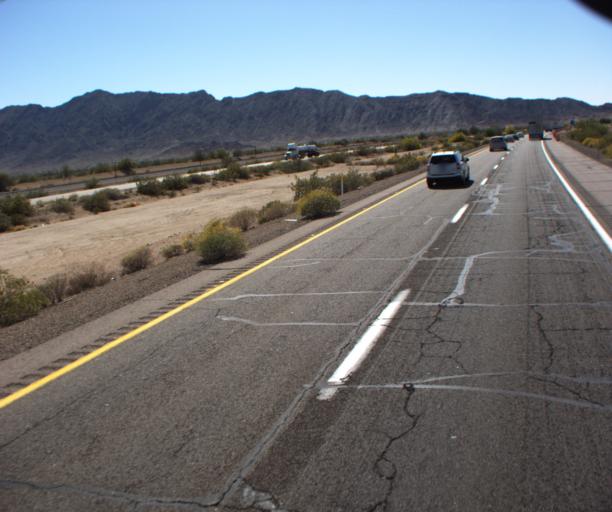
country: US
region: Arizona
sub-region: Yuma County
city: Wellton
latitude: 32.7330
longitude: -113.7090
